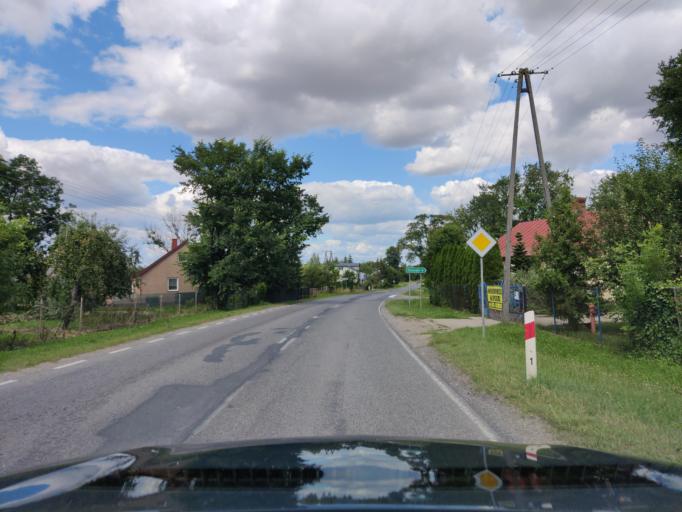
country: PL
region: Masovian Voivodeship
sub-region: Powiat wegrowski
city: Grebkow
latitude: 52.2931
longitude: 21.9283
